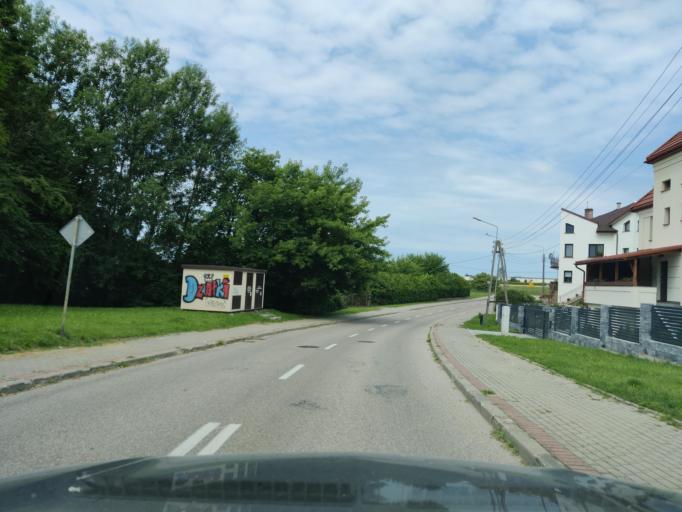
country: PL
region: Podlasie
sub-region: Powiat zambrowski
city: Zambrow
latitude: 52.9910
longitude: 22.2369
